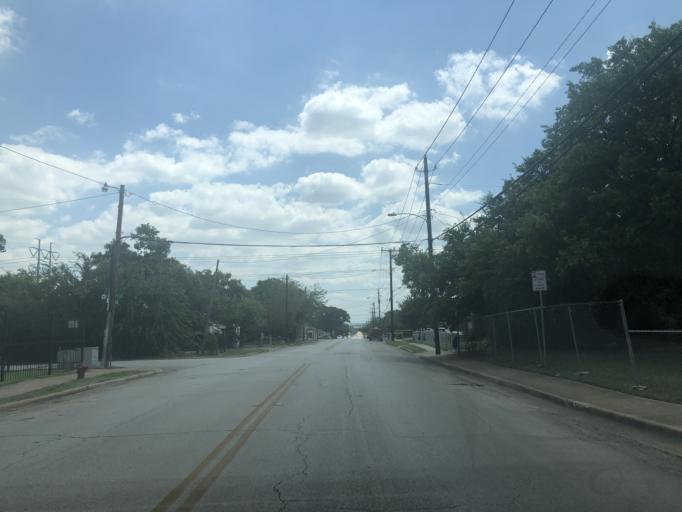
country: US
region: Texas
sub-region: Dallas County
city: Grand Prairie
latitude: 32.7351
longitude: -97.0361
